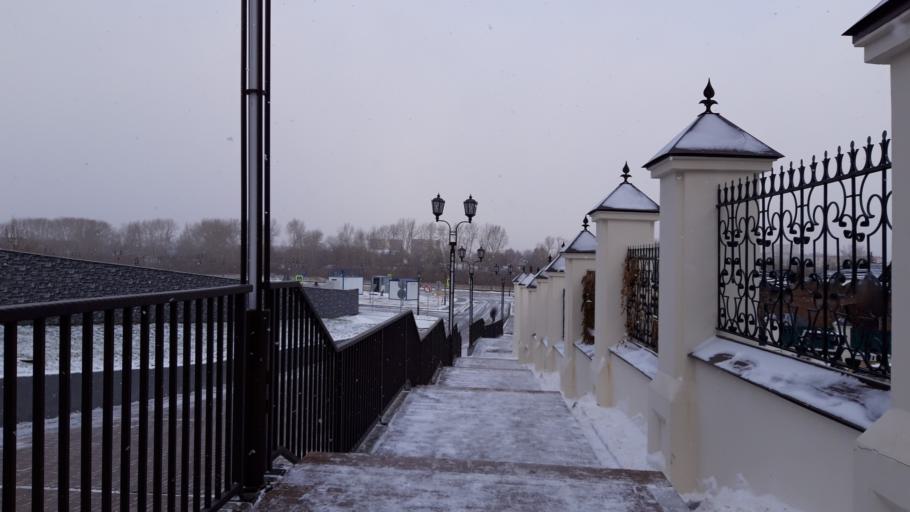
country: RU
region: Tjumen
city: Tyumen
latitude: 57.1612
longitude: 65.5504
